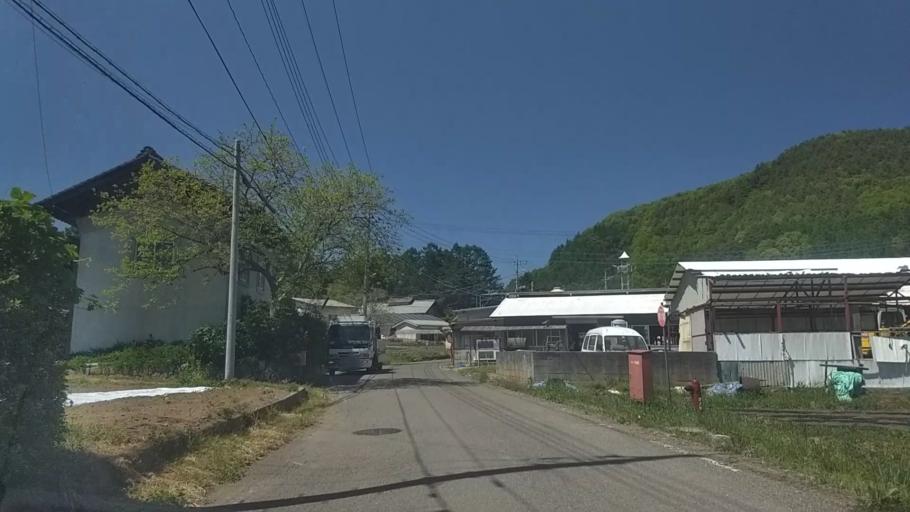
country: JP
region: Yamanashi
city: Nirasaki
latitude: 35.8737
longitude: 138.4529
